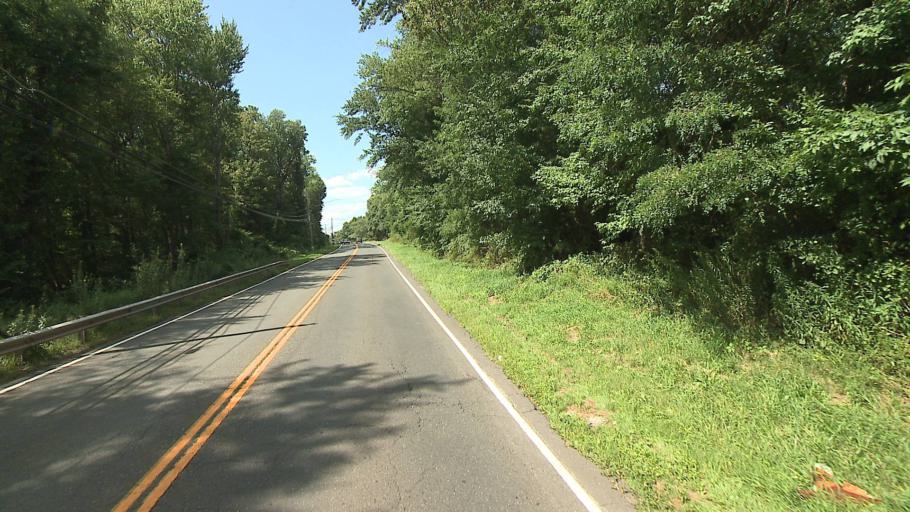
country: US
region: Connecticut
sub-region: Hartford County
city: Broad Brook
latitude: 41.9286
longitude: -72.5519
